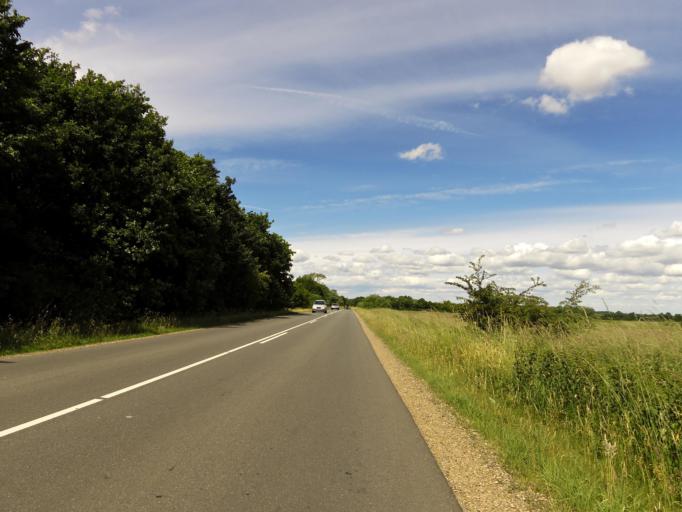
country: DK
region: South Denmark
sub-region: Esbjerg Kommune
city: Ribe
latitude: 55.2813
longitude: 8.7890
